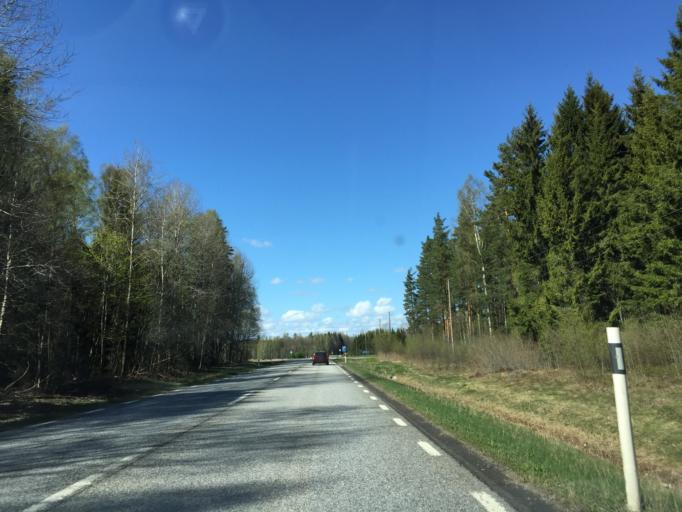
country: SE
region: OErebro
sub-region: Hallsbergs Kommun
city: Skollersta
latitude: 59.1400
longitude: 15.2770
